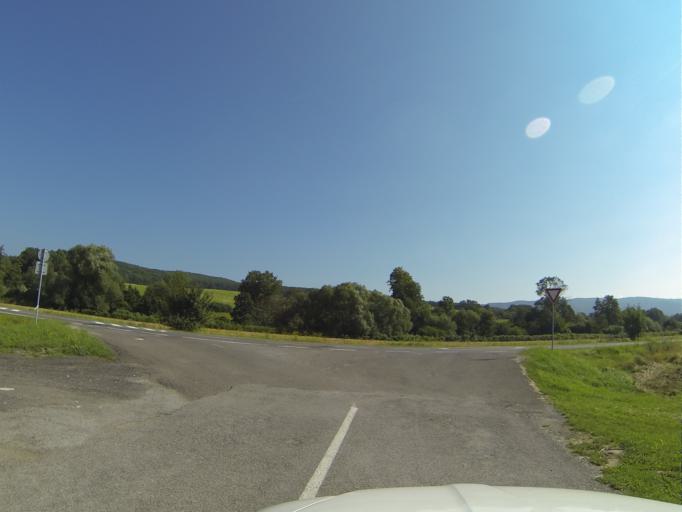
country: SK
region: Nitriansky
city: Prievidza
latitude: 48.7817
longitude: 18.6839
